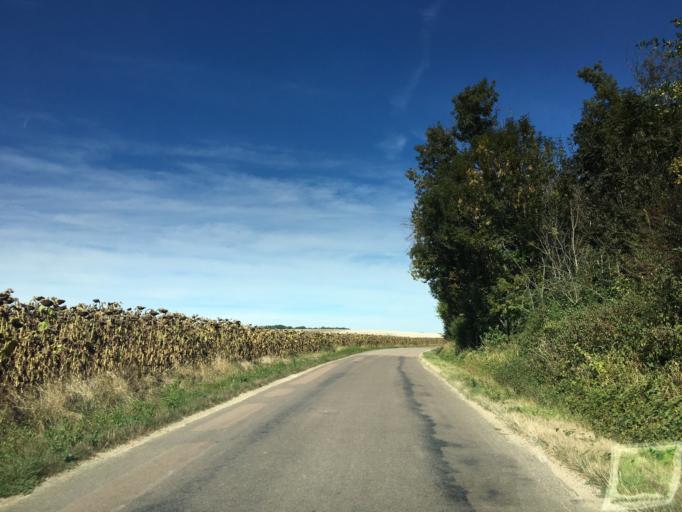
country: FR
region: Bourgogne
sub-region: Departement de l'Yonne
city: Fleury-la-Vallee
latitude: 47.8639
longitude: 3.4402
